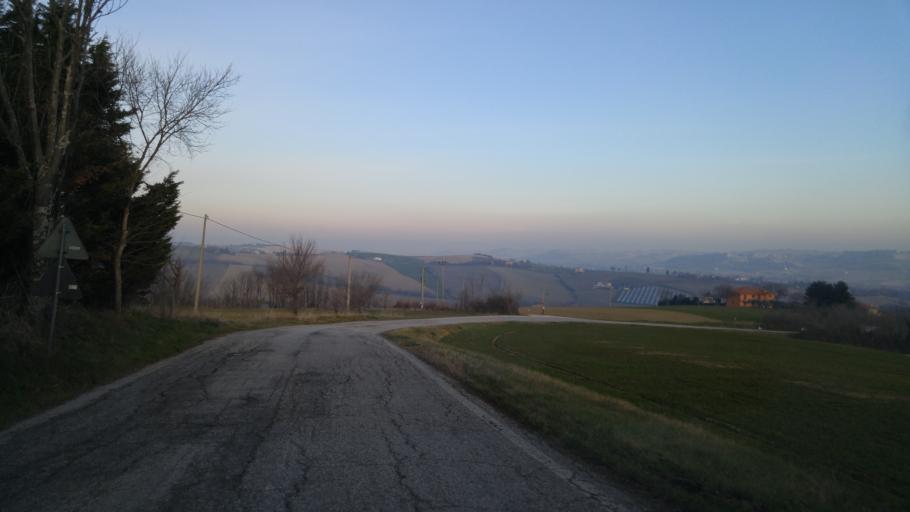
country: IT
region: The Marches
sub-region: Provincia di Pesaro e Urbino
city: Monte Porzio
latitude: 43.6978
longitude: 13.0238
